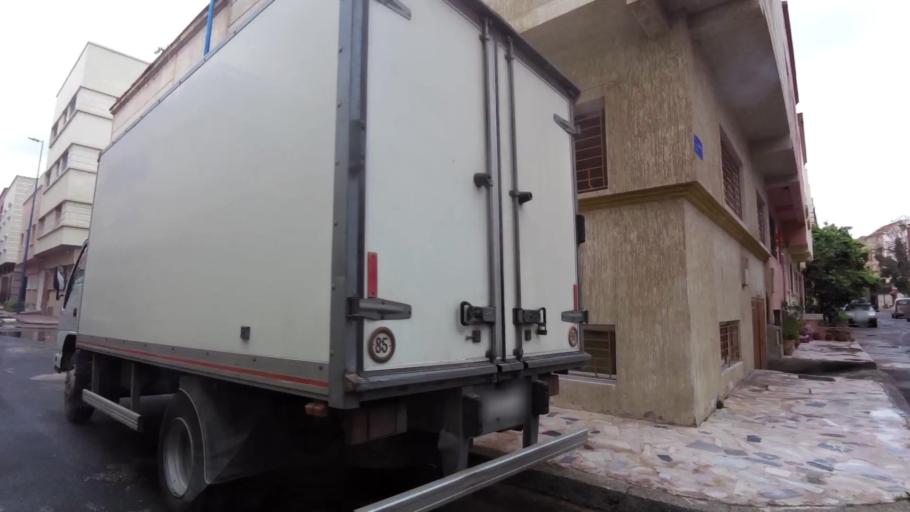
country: MA
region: Grand Casablanca
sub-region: Casablanca
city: Casablanca
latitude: 33.5395
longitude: -7.6500
